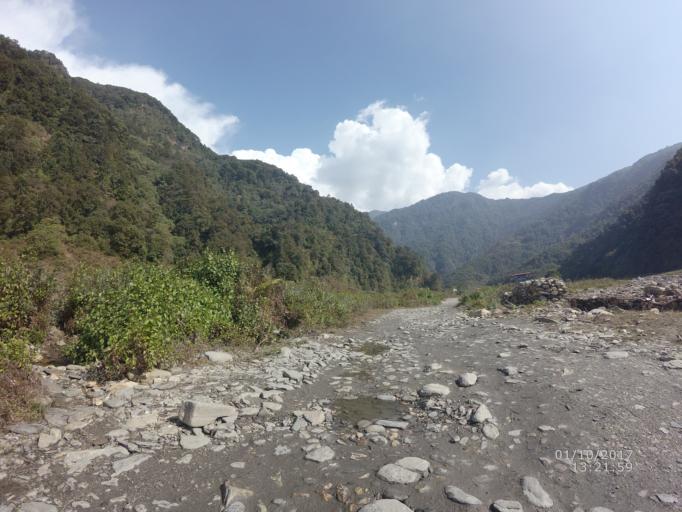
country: NP
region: Western Region
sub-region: Gandaki Zone
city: Pokhara
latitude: 28.3301
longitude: 83.9753
